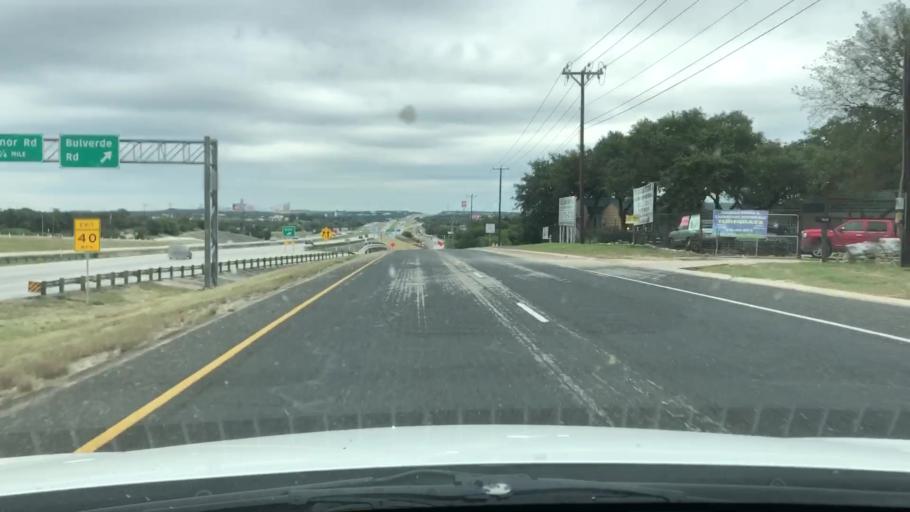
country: US
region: Texas
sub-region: Bexar County
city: Hollywood Park
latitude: 29.6001
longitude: -98.4249
